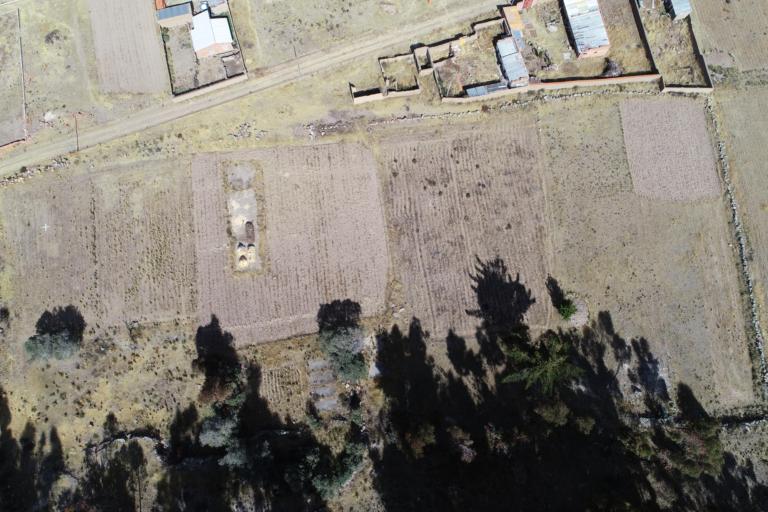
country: BO
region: La Paz
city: Achacachi
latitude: -15.8944
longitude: -68.9069
